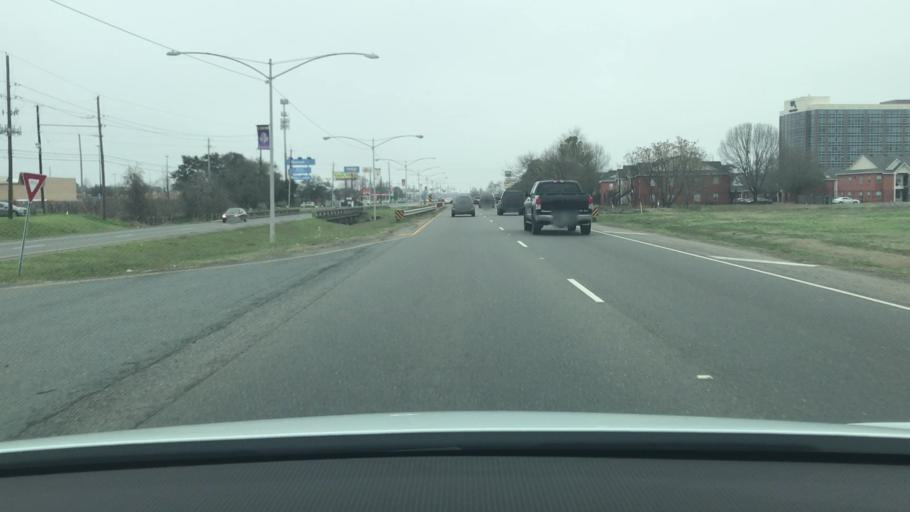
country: US
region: Louisiana
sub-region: Bossier Parish
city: Bossier City
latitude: 32.4279
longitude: -93.7095
